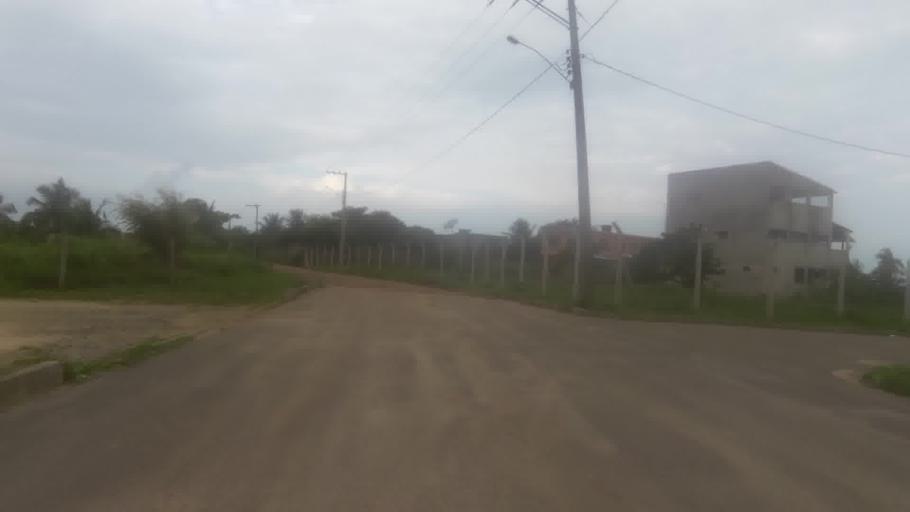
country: BR
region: Espirito Santo
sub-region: Piuma
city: Piuma
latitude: -20.7999
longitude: -40.5895
